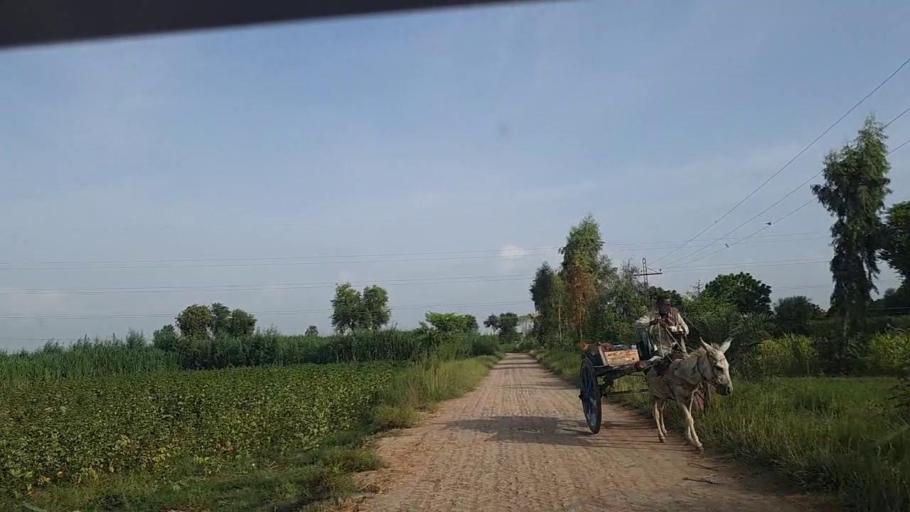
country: PK
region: Sindh
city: Ghotki
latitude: 27.9807
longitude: 69.2567
